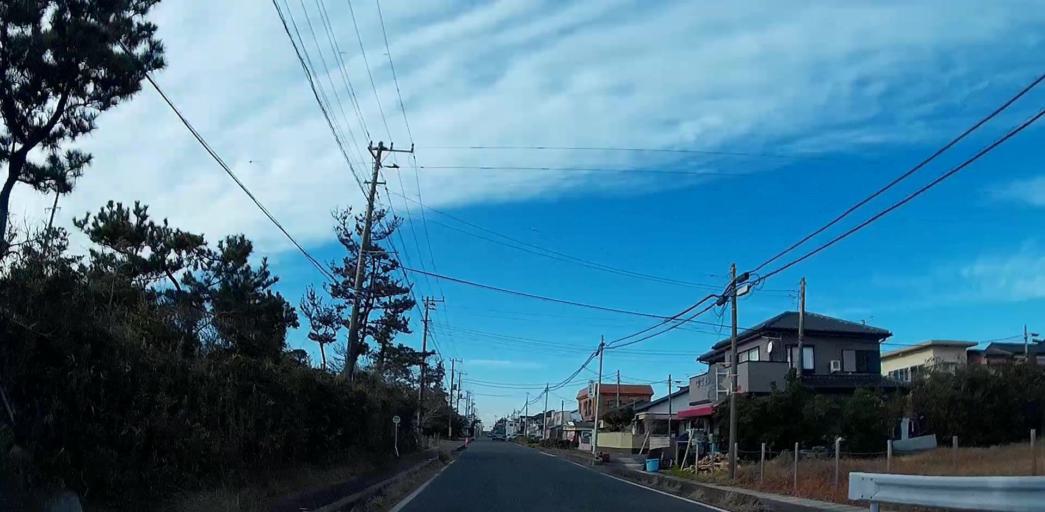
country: JP
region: Chiba
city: Hasaki
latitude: 35.7451
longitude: 140.8372
